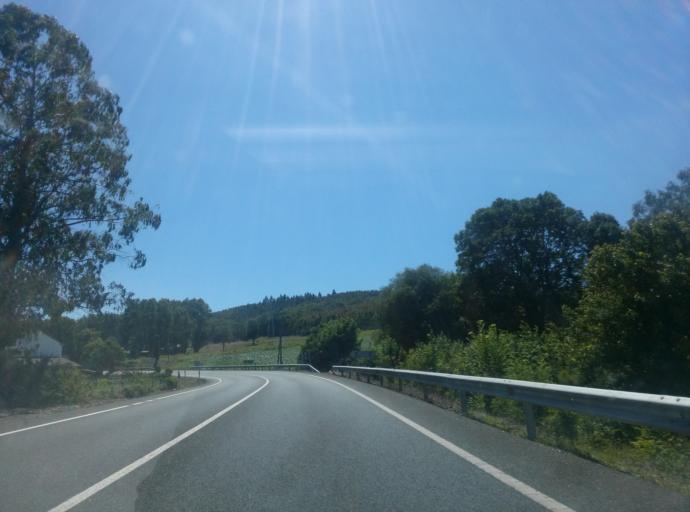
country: ES
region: Galicia
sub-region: Provincia de Lugo
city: Meira
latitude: 43.2152
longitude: -7.3234
